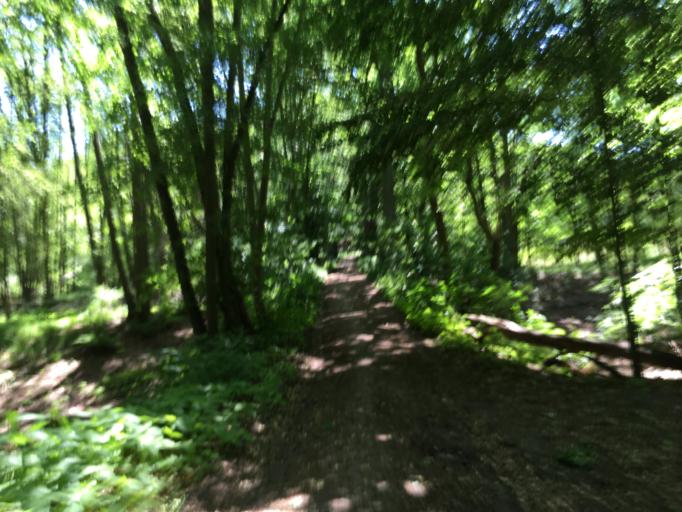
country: DE
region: Brandenburg
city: Zehdenick
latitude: 52.9063
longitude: 13.2397
